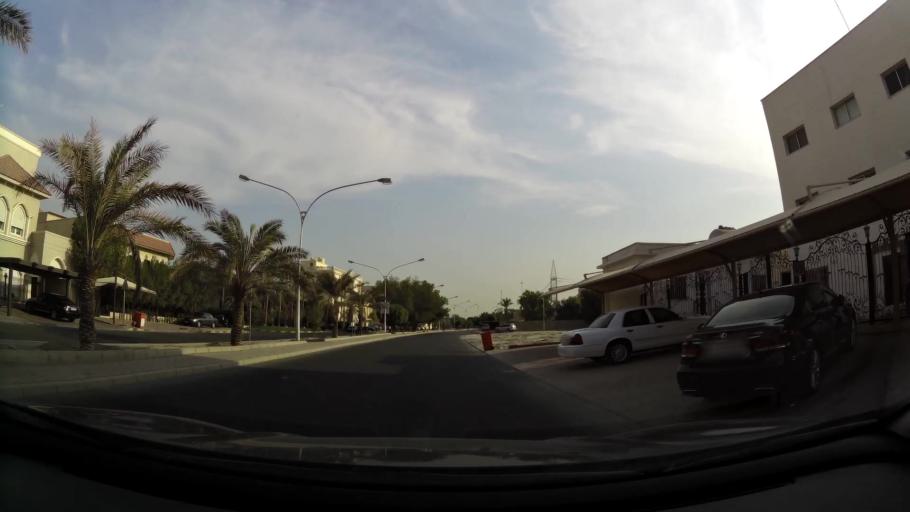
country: KW
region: Muhafazat Hawalli
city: Hawalli
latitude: 29.3093
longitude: 48.0147
